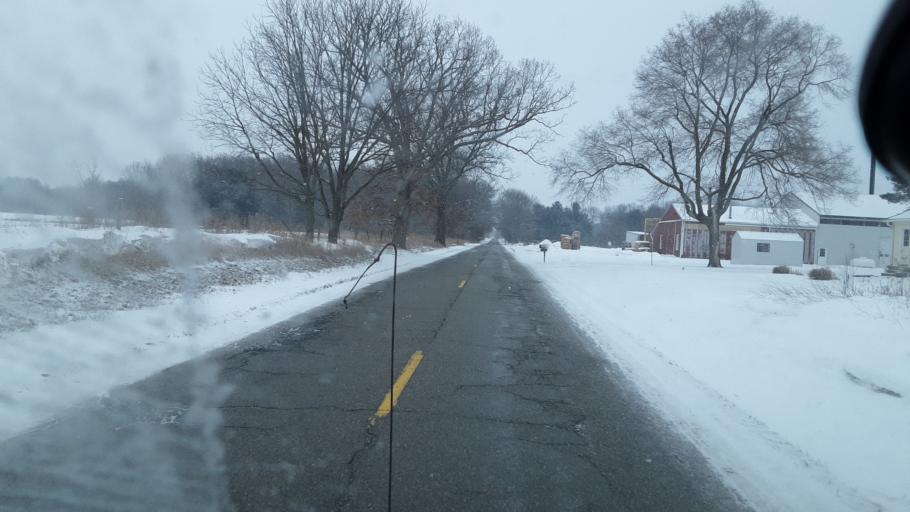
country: US
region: Michigan
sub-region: Ingham County
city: Leslie
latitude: 42.4896
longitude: -84.3515
